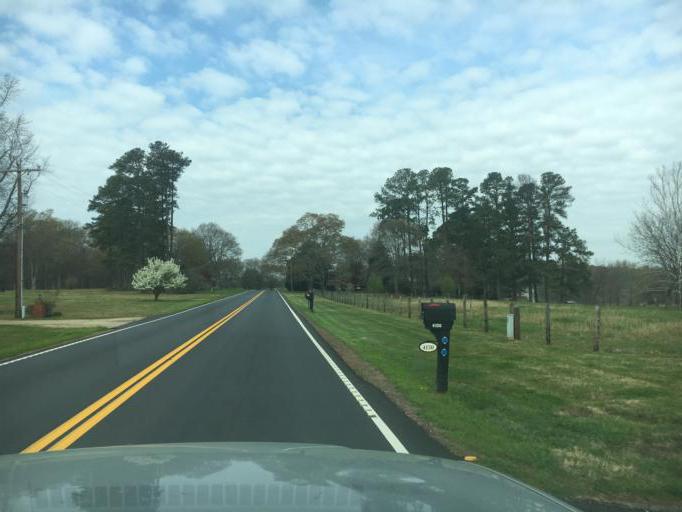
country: US
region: South Carolina
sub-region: Spartanburg County
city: Inman
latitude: 35.0248
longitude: -82.0893
